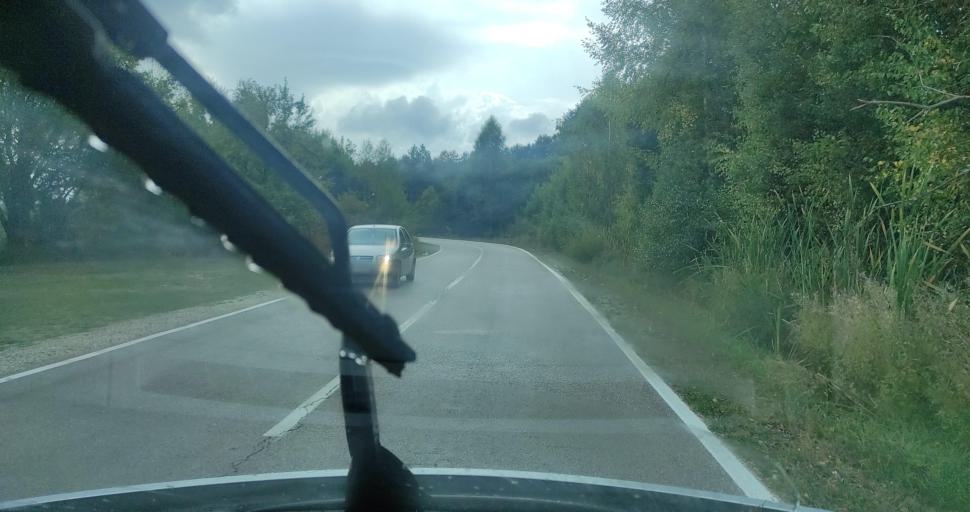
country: RS
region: Central Serbia
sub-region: Jablanicki Okrug
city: Crna Trava
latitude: 42.7046
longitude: 22.3270
